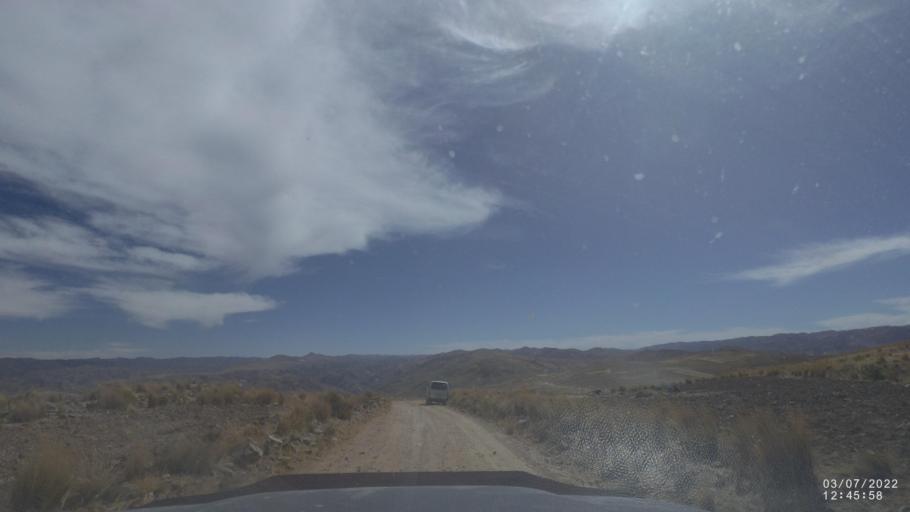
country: BO
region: Cochabamba
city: Irpa Irpa
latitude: -17.7750
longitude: -66.6377
